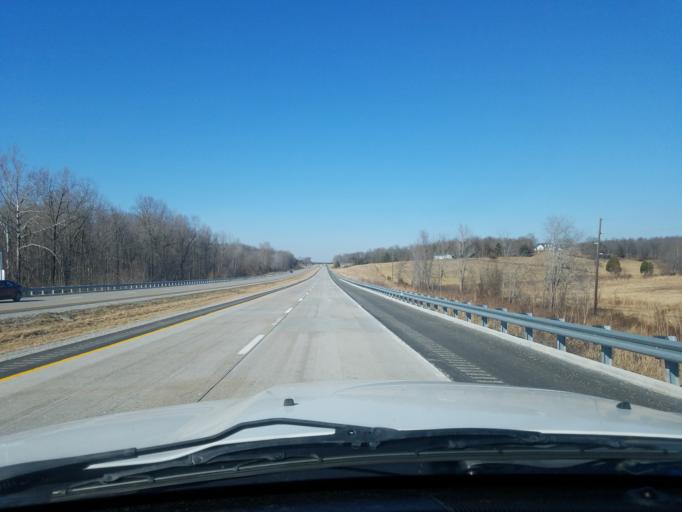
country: US
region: Kentucky
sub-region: Ohio County
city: Beaver Dam
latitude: 37.4020
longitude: -86.8216
